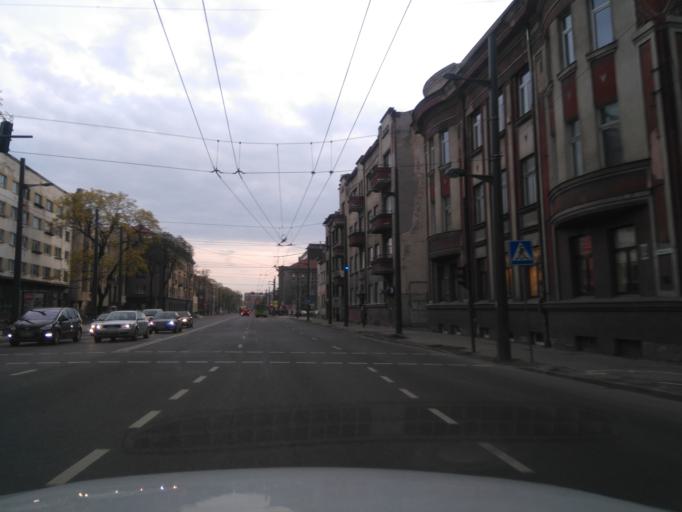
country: LT
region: Kauno apskritis
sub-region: Kaunas
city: Kaunas
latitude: 54.8969
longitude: 23.9252
